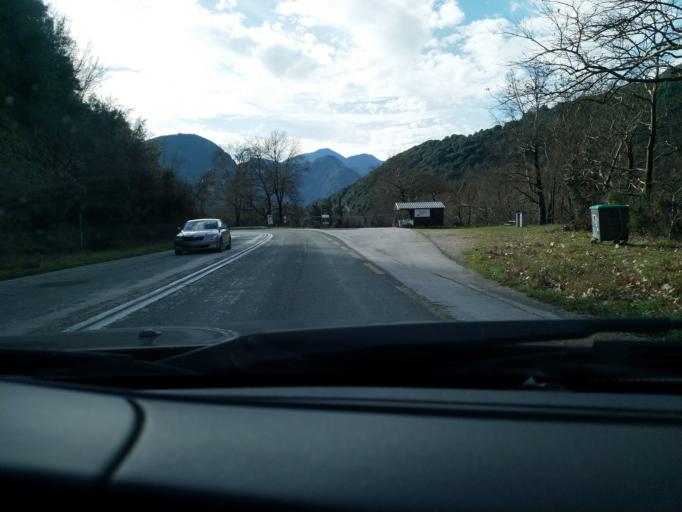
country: GR
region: Epirus
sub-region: Nomos Ioanninon
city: Agia Kyriaki
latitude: 39.4242
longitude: 20.8435
